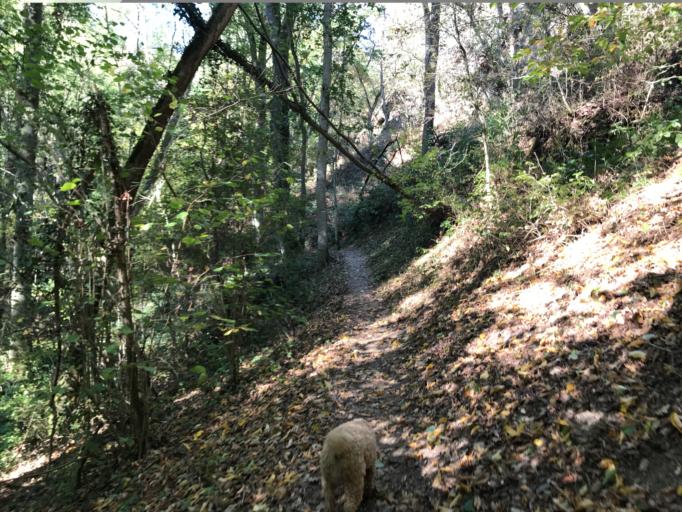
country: DE
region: Rheinland-Pfalz
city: Lonnig
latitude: 50.3023
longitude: 7.4275
